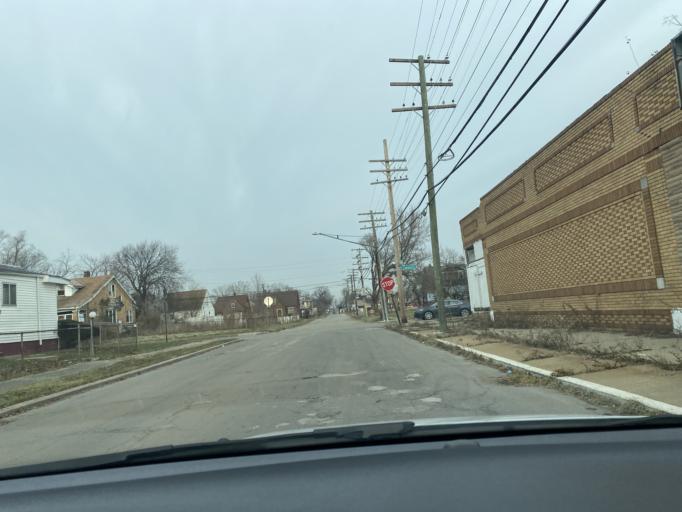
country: US
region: Michigan
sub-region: Wayne County
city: Highland Park
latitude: 42.3790
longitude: -83.1292
